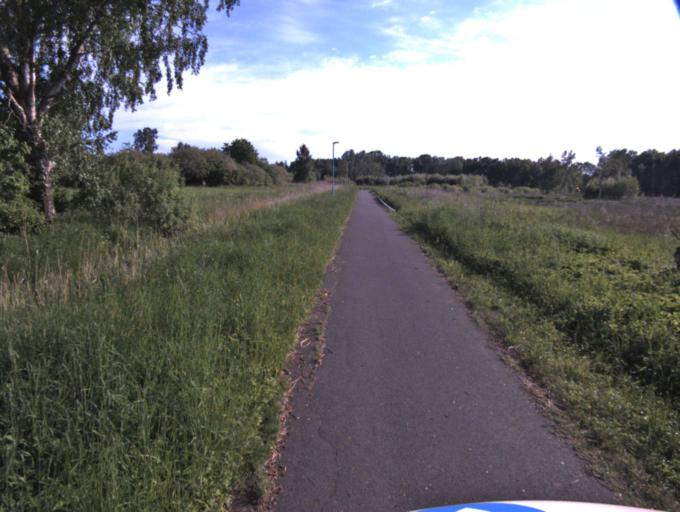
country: SE
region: Skane
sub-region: Kristianstads Kommun
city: Kristianstad
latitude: 56.0453
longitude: 14.1938
